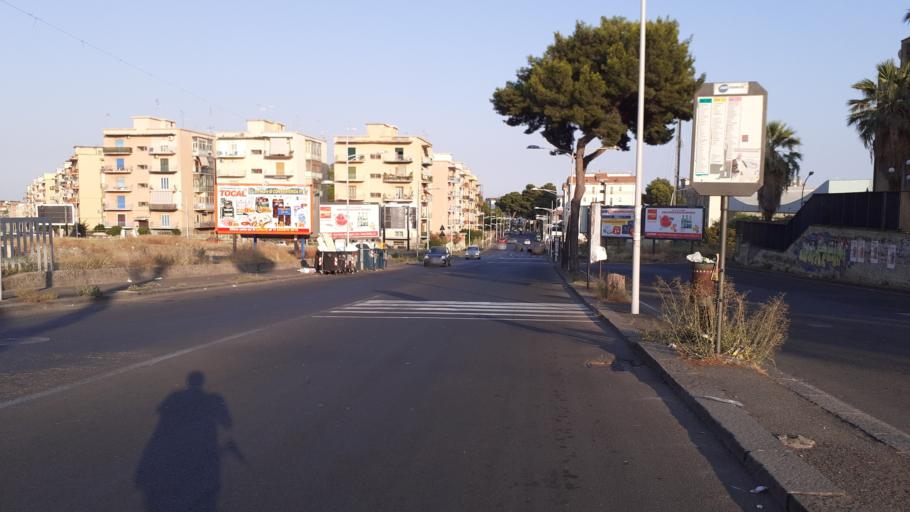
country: IT
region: Sicily
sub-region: Catania
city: Catania
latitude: 37.5046
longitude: 15.0553
